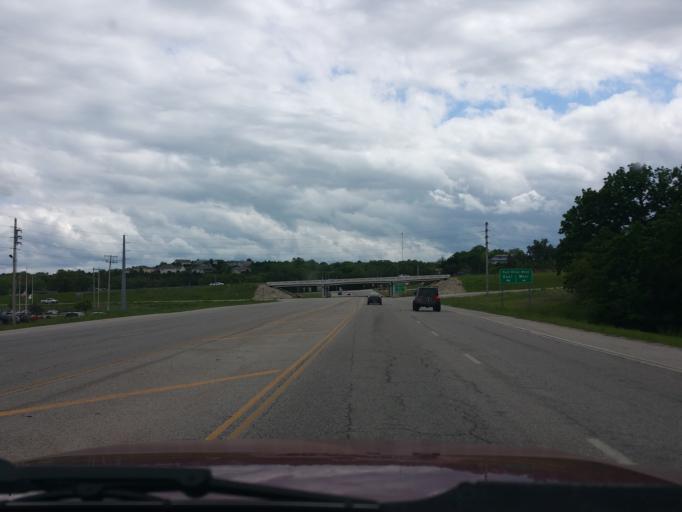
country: US
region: Kansas
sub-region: Riley County
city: Manhattan
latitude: 39.1721
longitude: -96.6038
